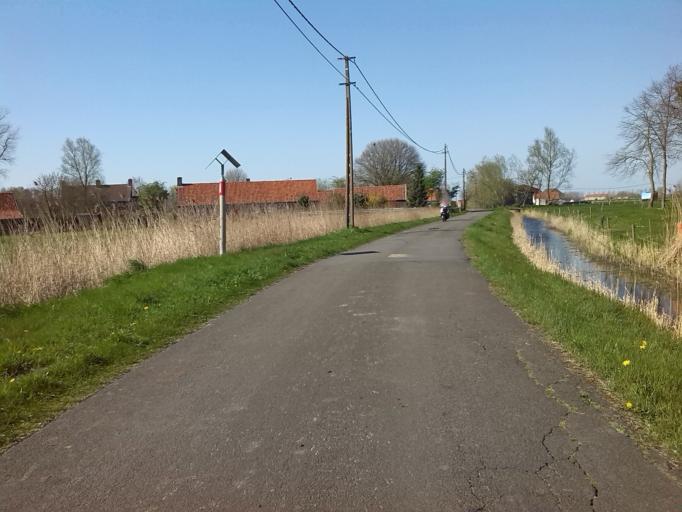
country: BE
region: Flanders
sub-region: Provincie West-Vlaanderen
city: Zuienkerke
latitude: 51.2243
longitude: 3.1608
